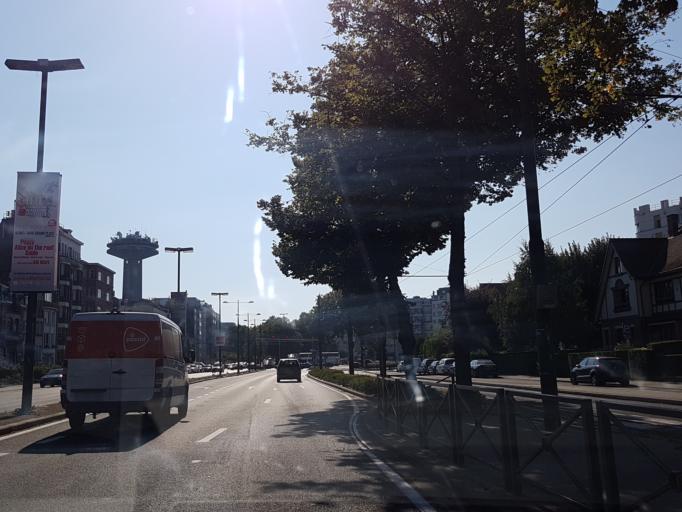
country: BE
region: Brussels Capital
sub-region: Bruxelles-Capitale
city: Brussels
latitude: 50.8567
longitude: 4.3978
